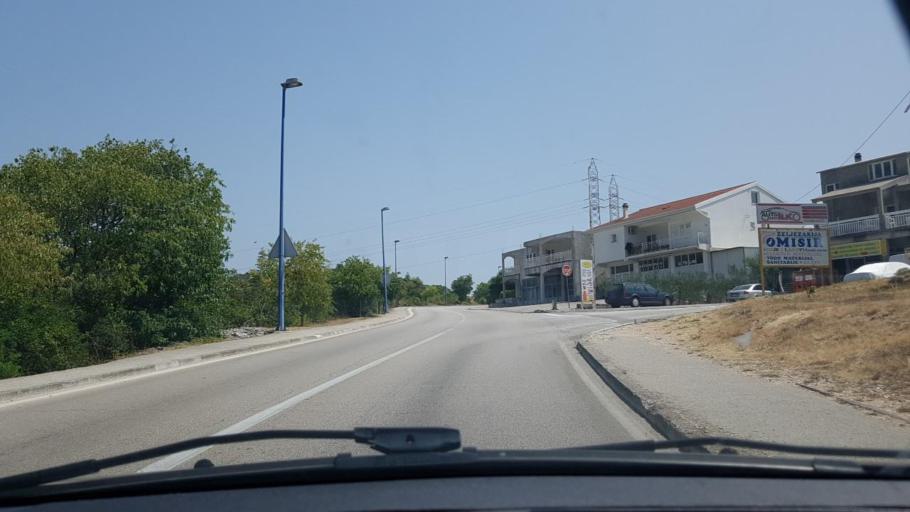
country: BA
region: Federation of Bosnia and Herzegovina
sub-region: Hercegovacko-Bosanski Kanton
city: Neum
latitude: 42.9266
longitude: 17.6192
